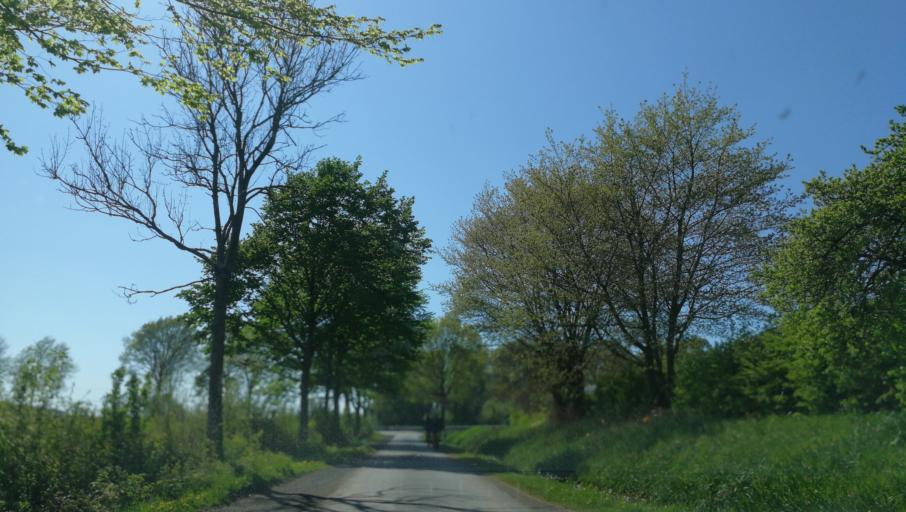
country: DE
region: North Rhine-Westphalia
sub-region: Regierungsbezirk Munster
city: Muenster
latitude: 51.9408
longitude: 7.5420
